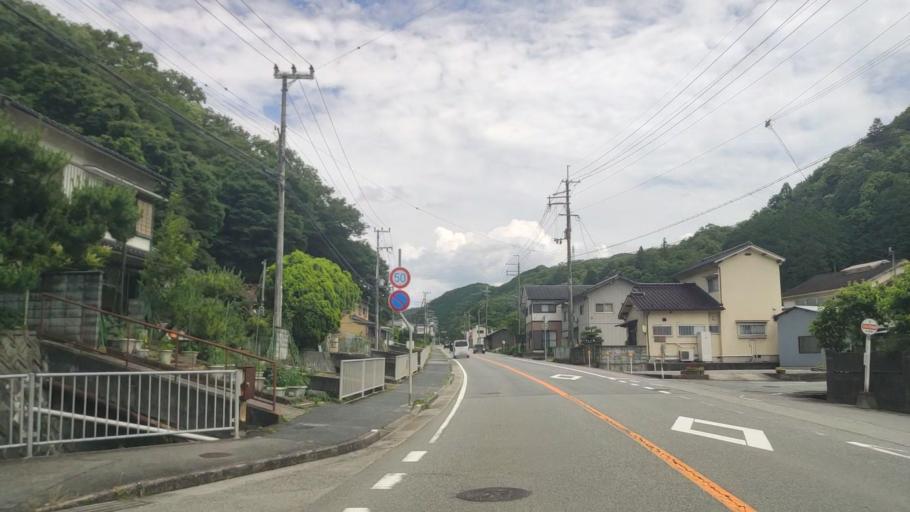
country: JP
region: Hyogo
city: Yamazakicho-nakabirose
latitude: 35.0053
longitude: 134.3644
